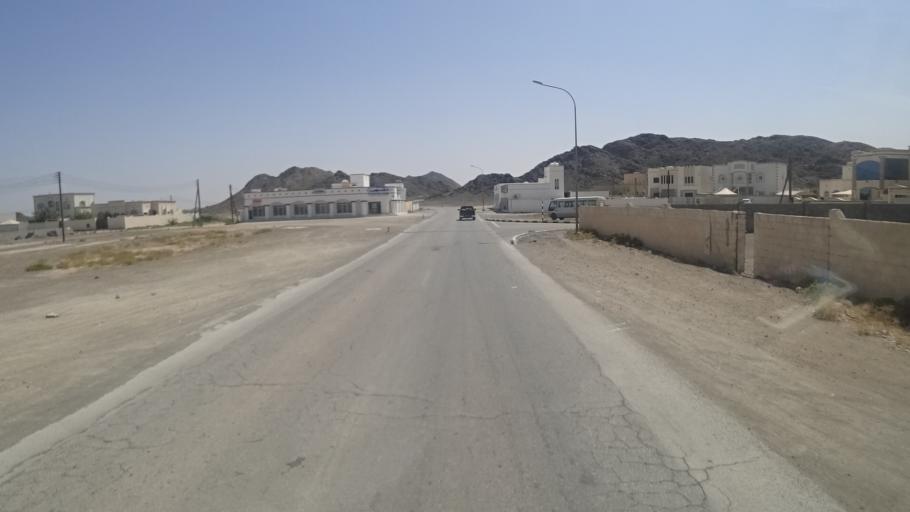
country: OM
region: Ash Sharqiyah
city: Ibra'
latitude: 22.6743
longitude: 58.5302
